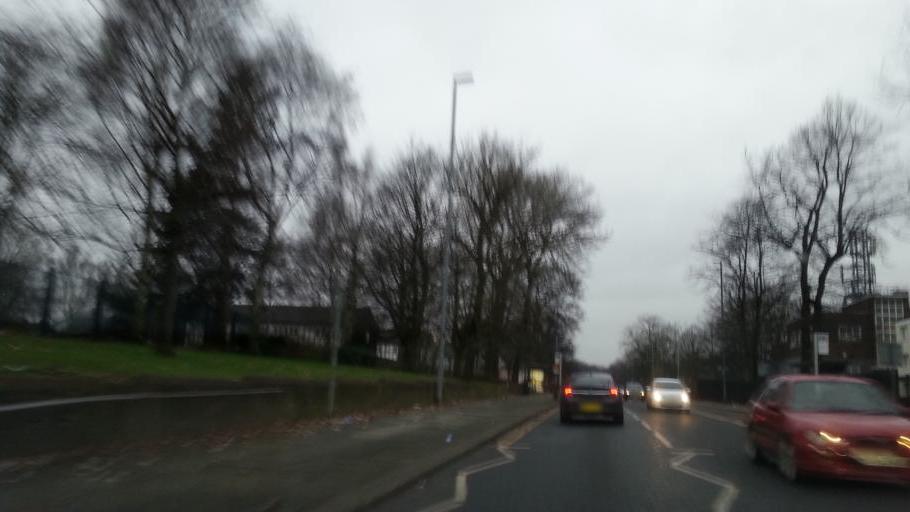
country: GB
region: England
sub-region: Manchester
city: Crumpsall
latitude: 53.5041
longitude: -2.2598
